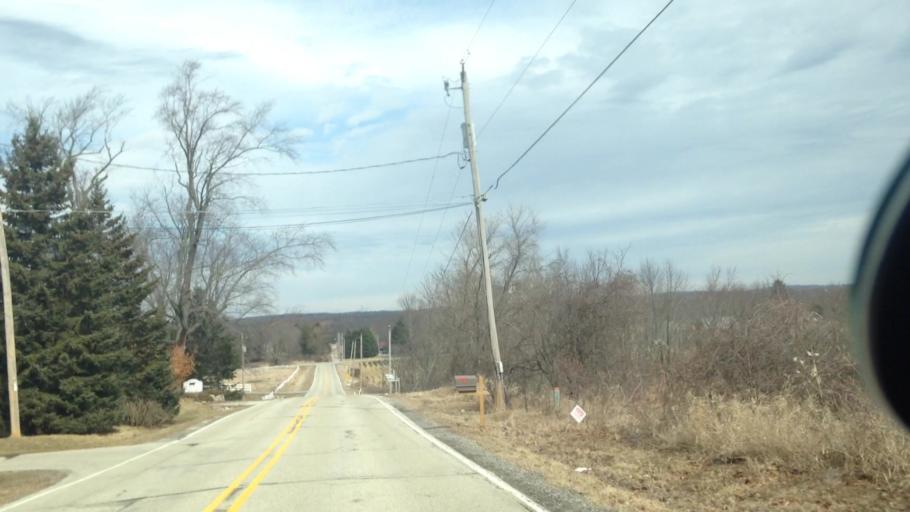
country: US
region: Wisconsin
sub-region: Waukesha County
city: Sussex
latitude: 43.1593
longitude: -88.2234
